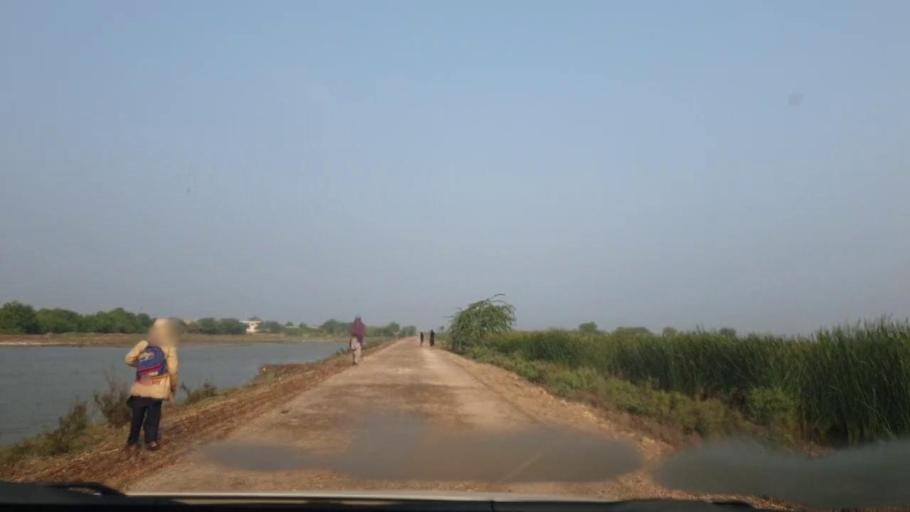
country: PK
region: Sindh
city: Tando Muhammad Khan
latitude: 25.0902
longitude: 68.4808
